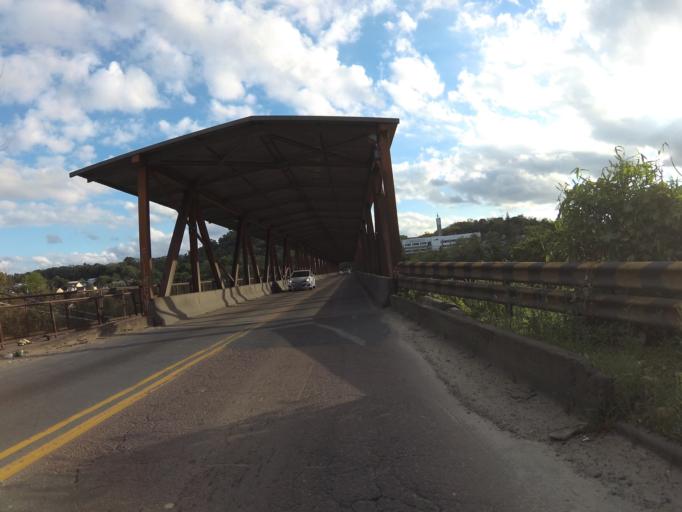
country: BR
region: Santa Catarina
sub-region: Blumenau
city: Blumenau
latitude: -26.8803
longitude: -49.1015
